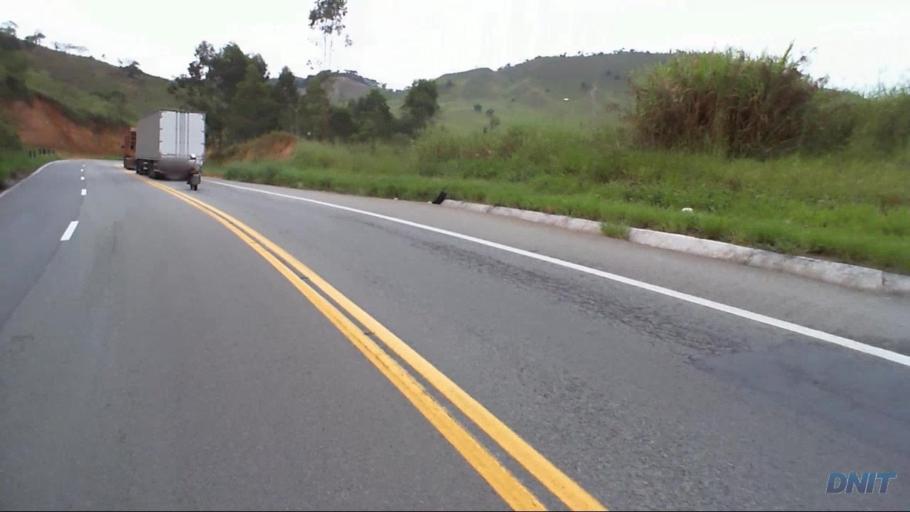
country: BR
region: Minas Gerais
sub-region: Nova Era
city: Nova Era
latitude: -19.6305
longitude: -42.8802
